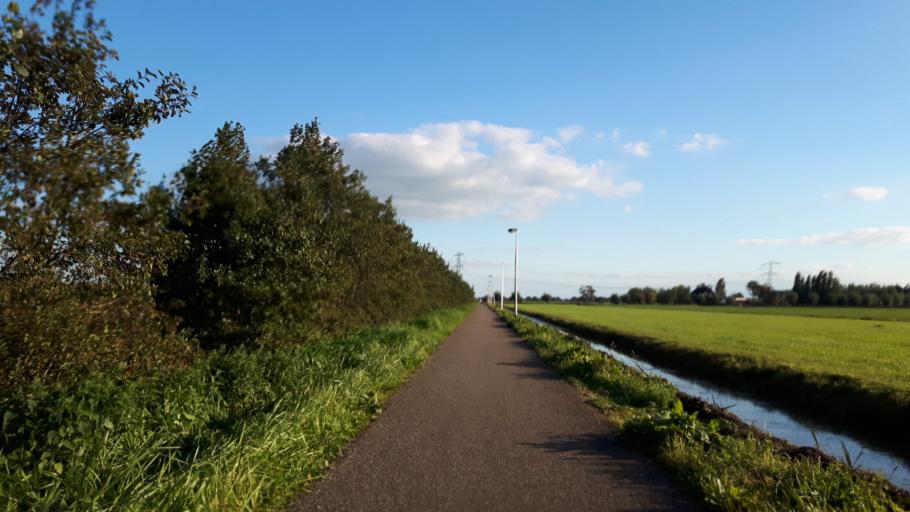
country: NL
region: Utrecht
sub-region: Gemeente Woerden
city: Woerden
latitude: 52.0618
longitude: 4.8694
